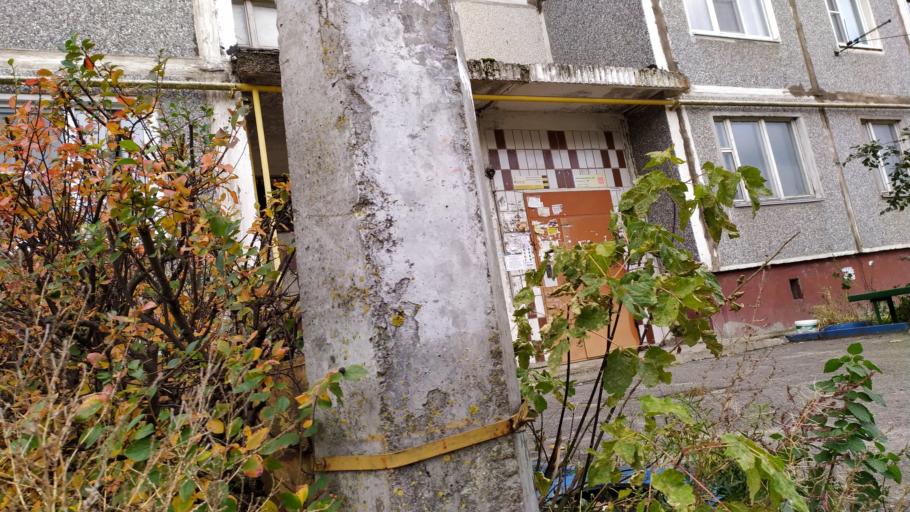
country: RU
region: Kursk
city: Kursk
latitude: 51.6510
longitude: 36.1466
